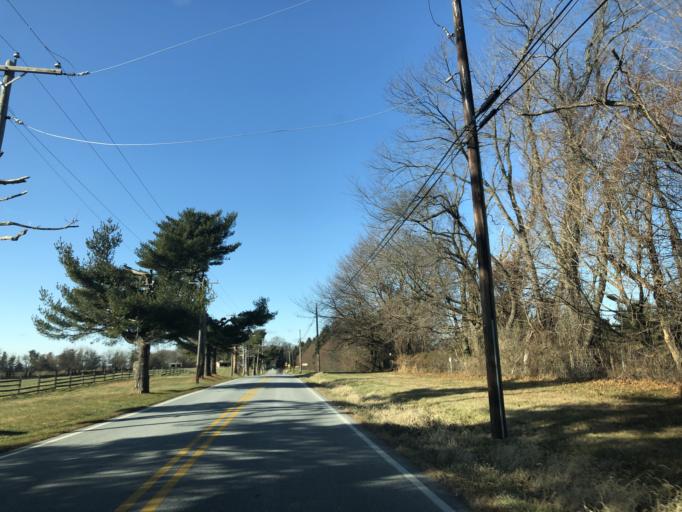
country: US
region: Pennsylvania
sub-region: Chester County
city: Upland
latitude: 39.8996
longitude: -75.7537
